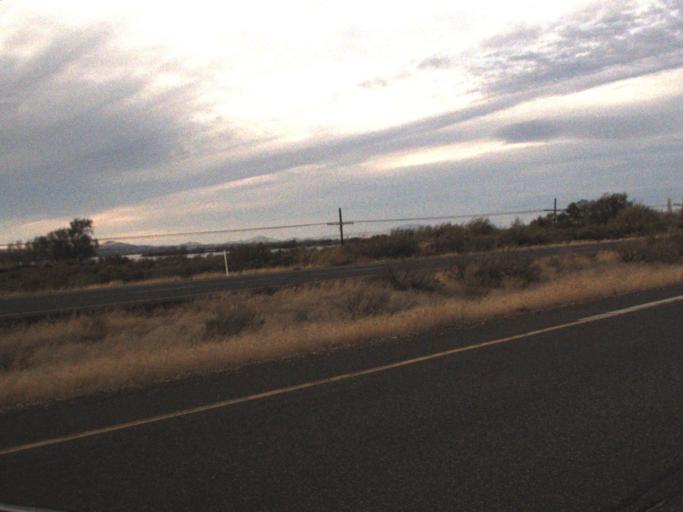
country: US
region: Washington
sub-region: Benton County
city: Finley
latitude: 46.1221
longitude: -118.9287
